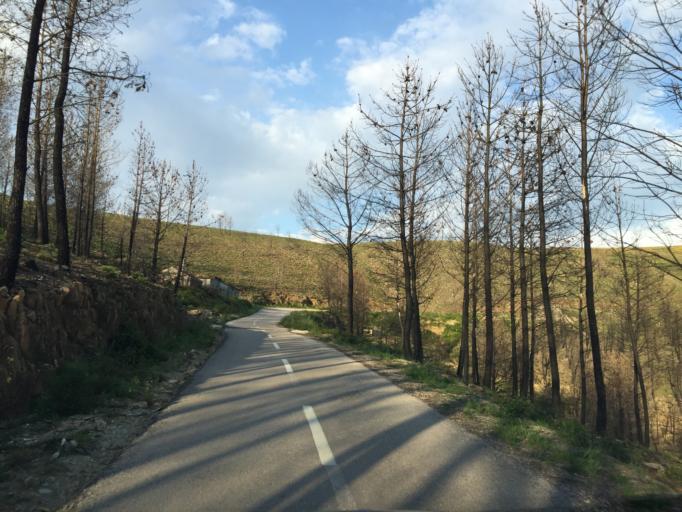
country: PT
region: Coimbra
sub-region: Pampilhosa da Serra
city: Pampilhosa da Serra
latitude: 40.1235
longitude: -8.0155
